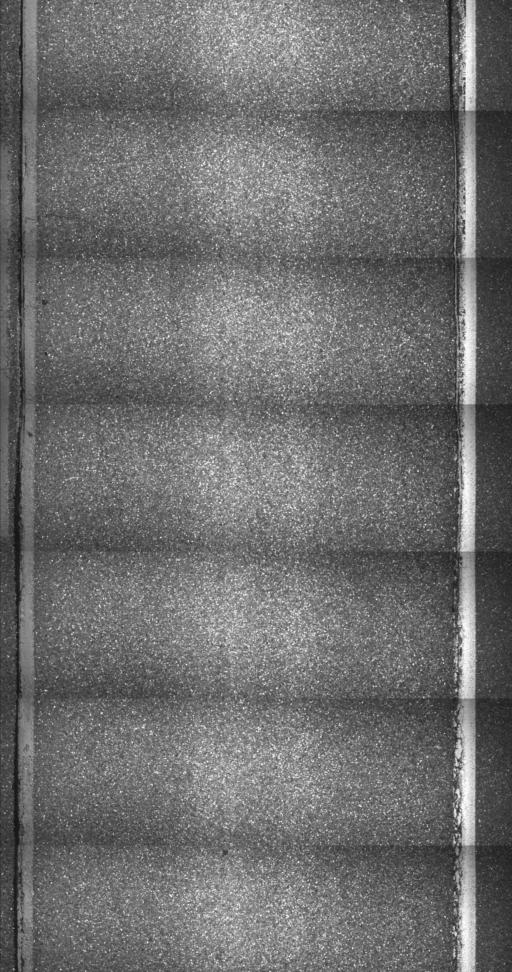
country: US
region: Vermont
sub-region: Rutland County
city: Fair Haven
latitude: 43.6797
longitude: -73.2890
